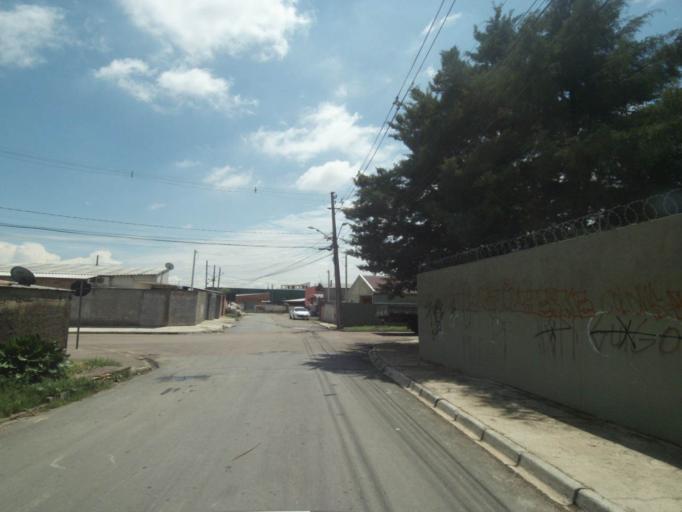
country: BR
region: Parana
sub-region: Pinhais
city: Pinhais
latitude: -25.4724
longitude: -49.1884
